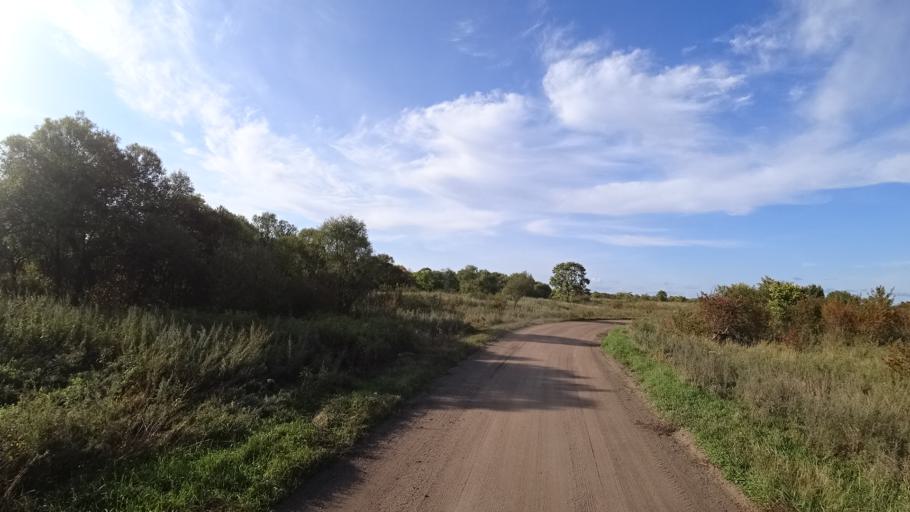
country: RU
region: Amur
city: Arkhara
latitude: 49.3505
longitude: 130.1008
